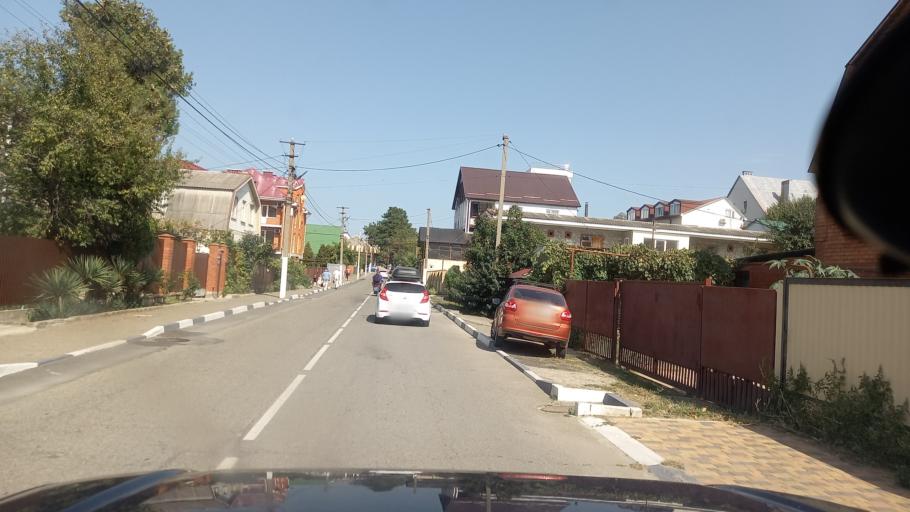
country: RU
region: Krasnodarskiy
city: Arkhipo-Osipovka
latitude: 44.3686
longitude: 38.5323
